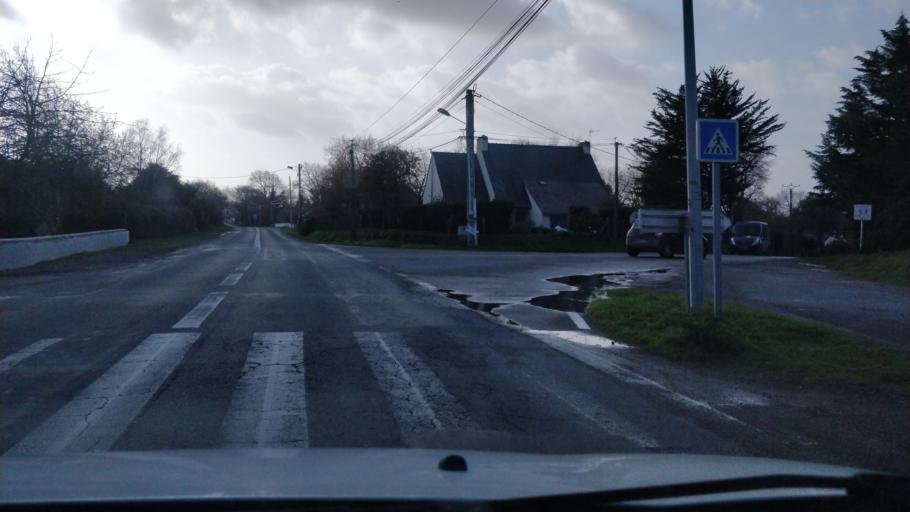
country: FR
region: Pays de la Loire
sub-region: Departement de la Loire-Atlantique
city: Guerande
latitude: 47.3556
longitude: -2.4330
